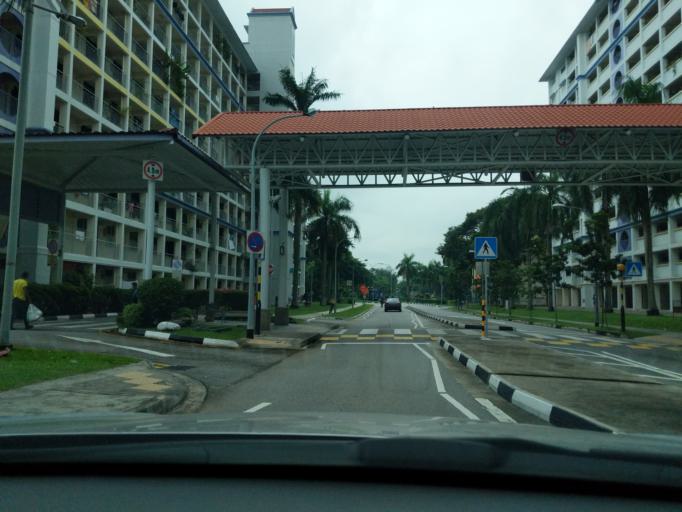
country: SG
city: Singapore
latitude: 1.3011
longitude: 103.8834
